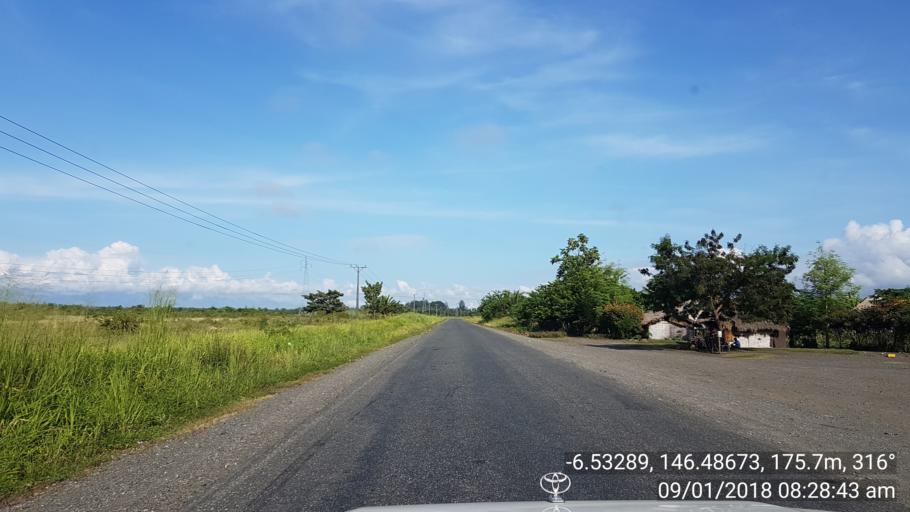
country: PG
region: Morobe
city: Lae
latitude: -6.5328
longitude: 146.4867
